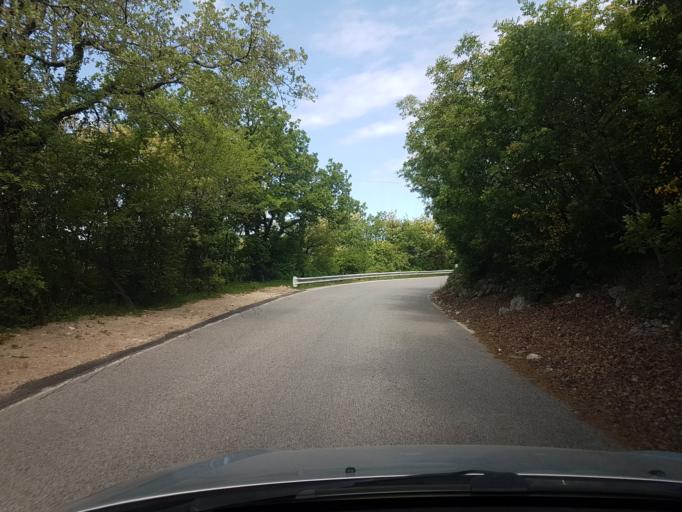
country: IT
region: Friuli Venezia Giulia
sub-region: Provincia di Trieste
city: Sistiana-Visogliano
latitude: 45.7800
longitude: 13.6476
